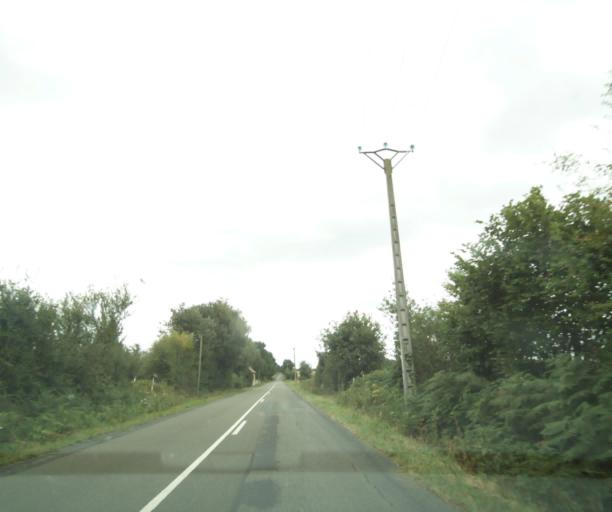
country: FR
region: Pays de la Loire
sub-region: Departement de la Sarthe
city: Precigne
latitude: 47.7346
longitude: -0.2664
